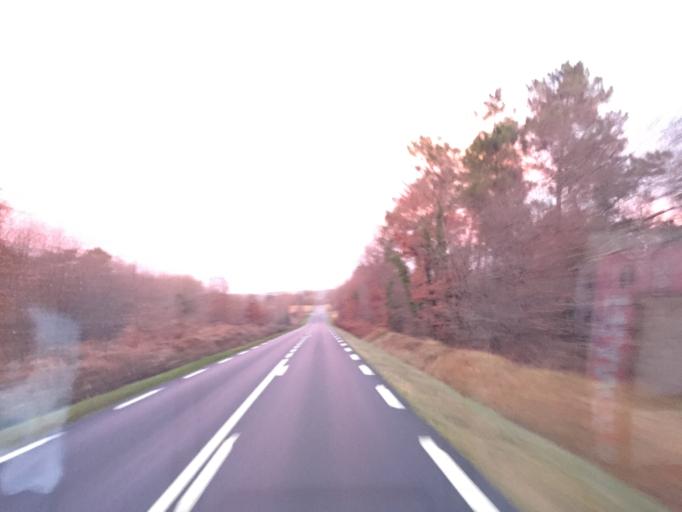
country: FR
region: Poitou-Charentes
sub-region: Departement de la Charente-Maritime
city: Montguyon
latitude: 45.1961
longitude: -0.1427
